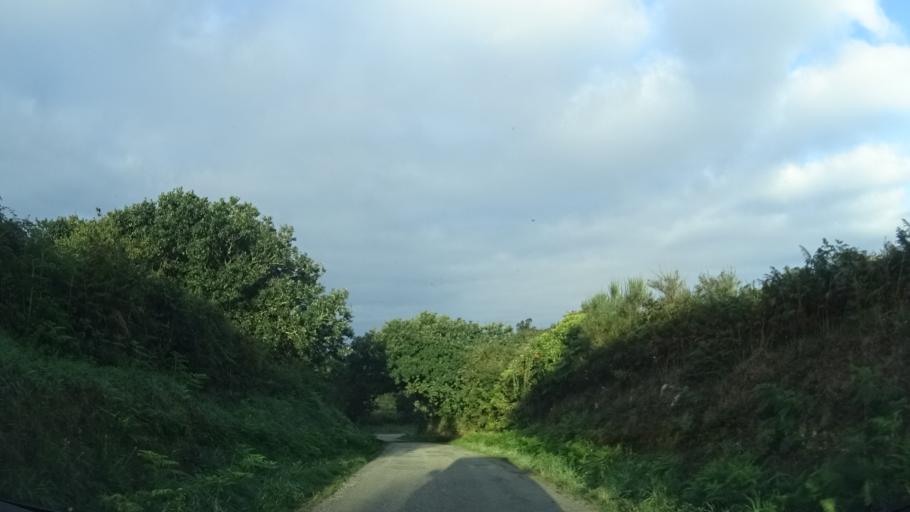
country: FR
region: Brittany
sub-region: Departement du Finistere
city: Lampaul-Plouarzel
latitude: 48.4598
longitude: -4.7576
